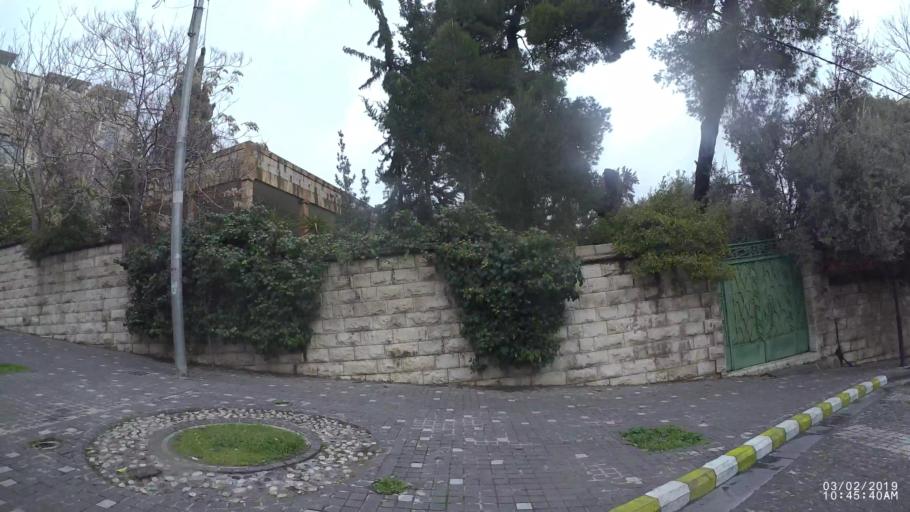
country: JO
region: Amman
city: Amman
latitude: 31.9495
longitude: 35.9315
